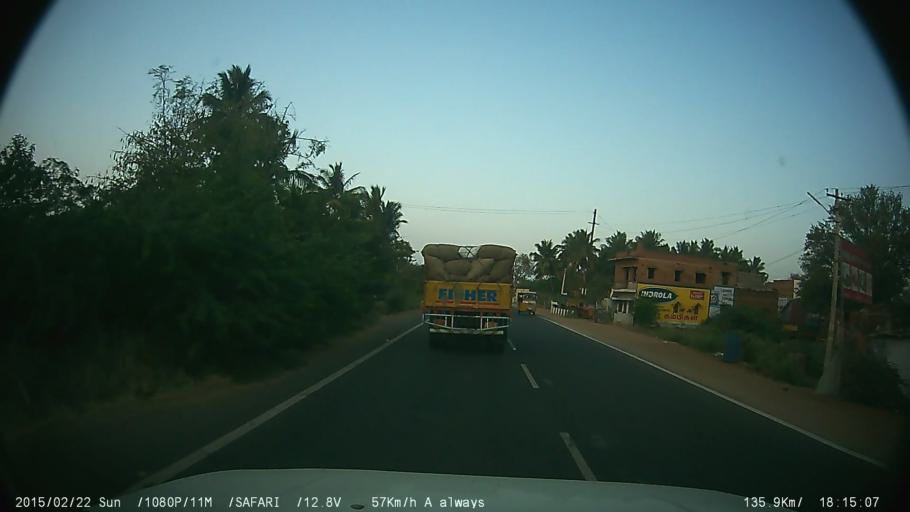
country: IN
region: Tamil Nadu
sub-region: Theni
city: Chinnamanur
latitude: 9.8649
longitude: 77.3914
